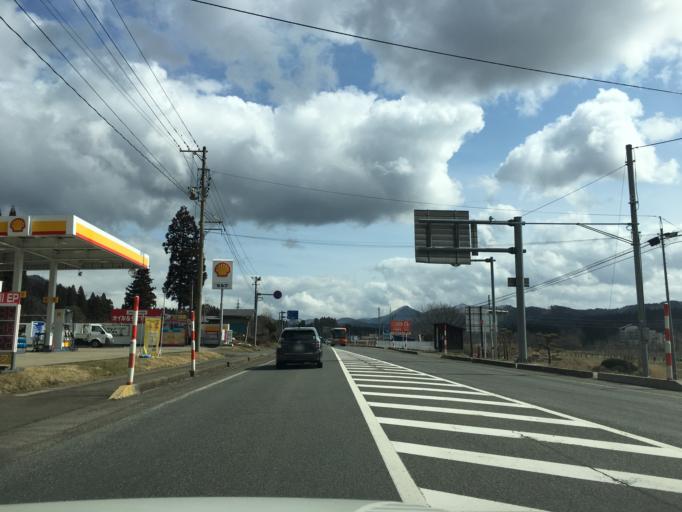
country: JP
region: Akita
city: Odate
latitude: 40.2304
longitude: 140.5929
